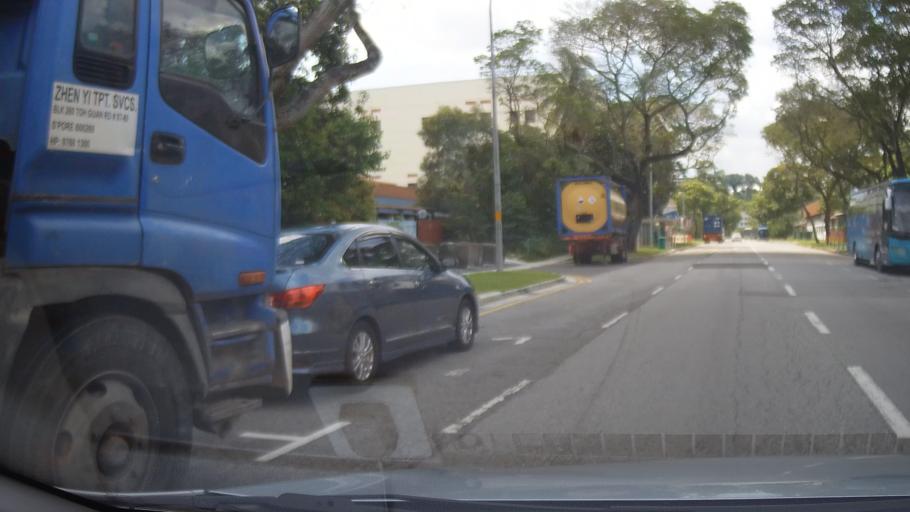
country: MY
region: Johor
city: Johor Bahru
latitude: 1.3246
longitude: 103.6891
